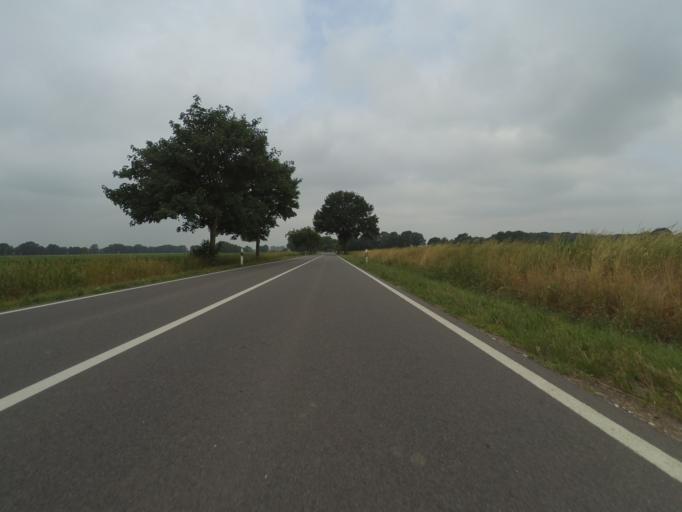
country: DE
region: Mecklenburg-Vorpommern
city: Domsuhl
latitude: 53.4826
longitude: 11.7543
